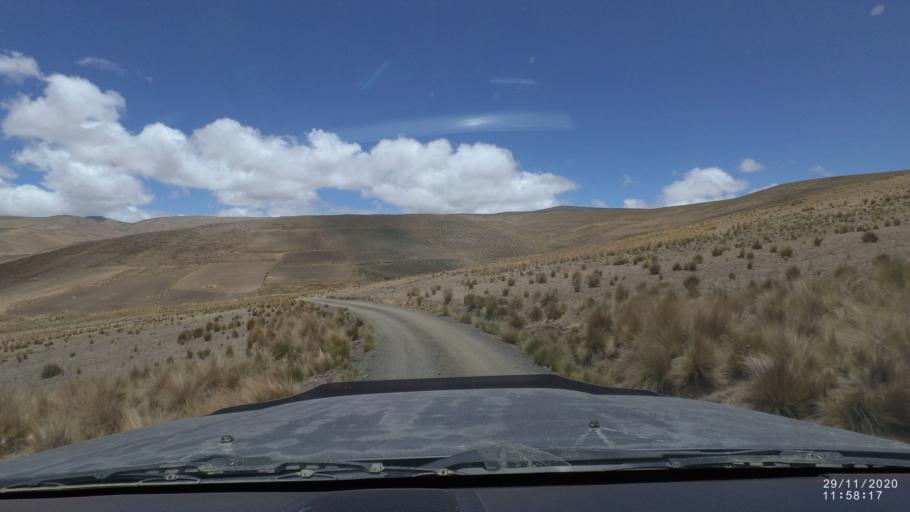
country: BO
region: Cochabamba
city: Cochabamba
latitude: -17.1562
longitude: -66.2750
